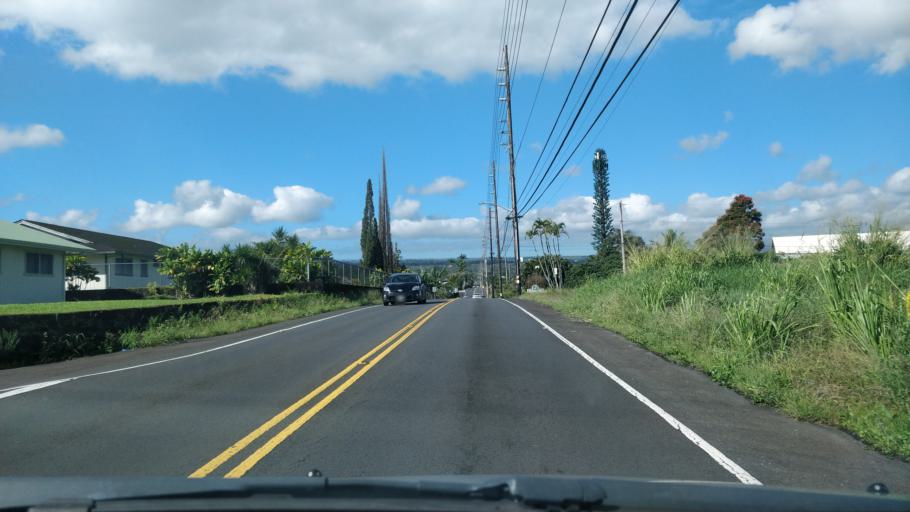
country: US
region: Hawaii
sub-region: Hawaii County
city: Hilo
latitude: 19.6829
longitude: -155.0939
